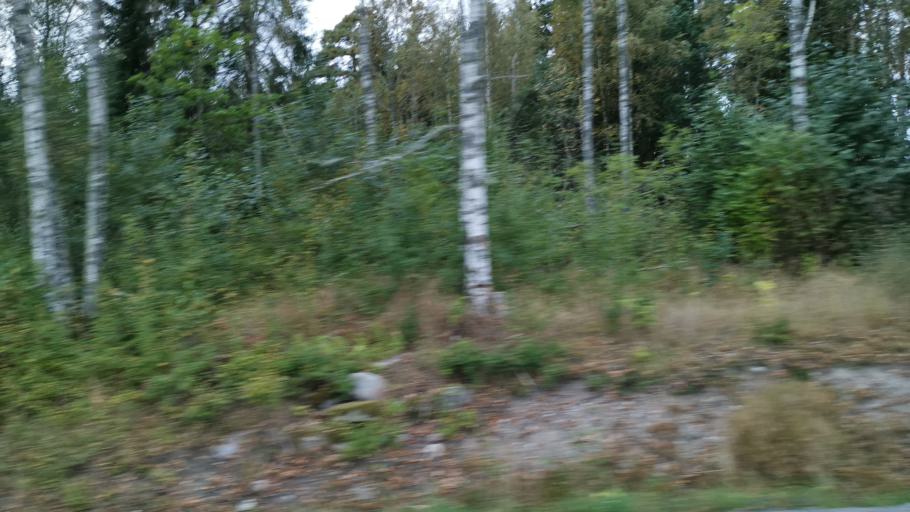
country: SE
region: Vaestra Goetaland
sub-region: Tanums Kommun
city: Tanumshede
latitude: 58.6912
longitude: 11.3353
